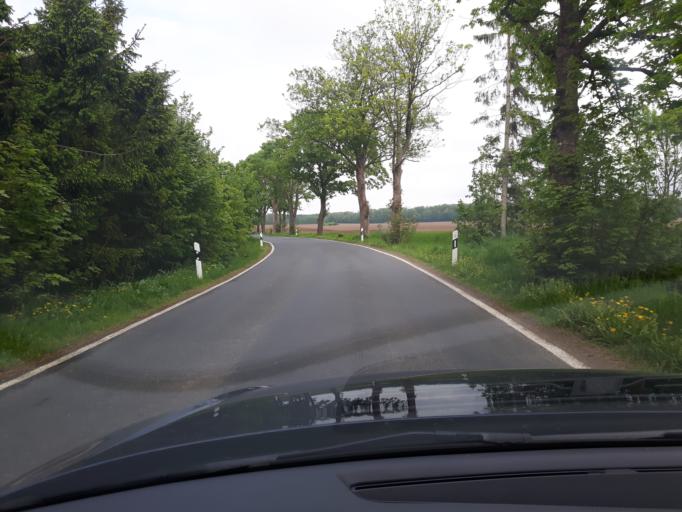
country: DE
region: Mecklenburg-Vorpommern
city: Velgast
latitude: 54.2186
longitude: 12.7350
